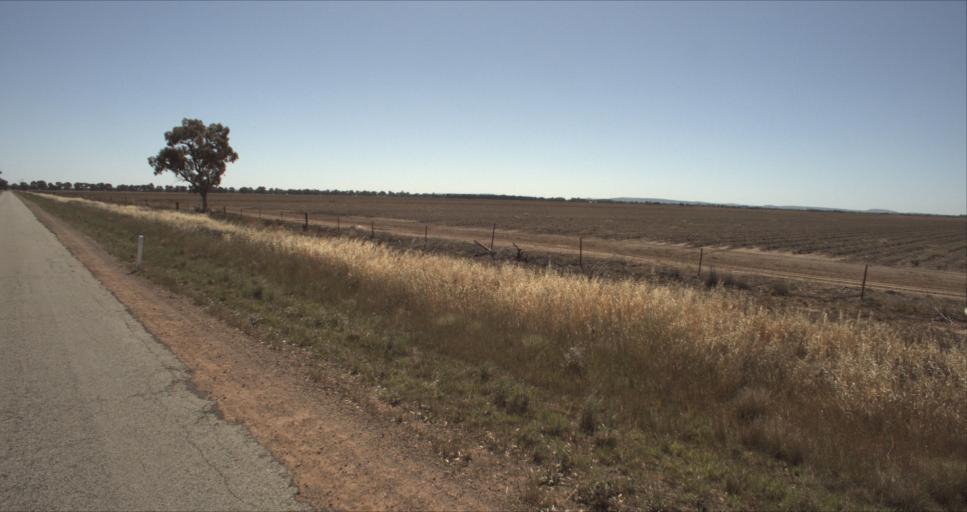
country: AU
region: New South Wales
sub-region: Leeton
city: Leeton
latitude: -34.5632
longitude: 146.3123
